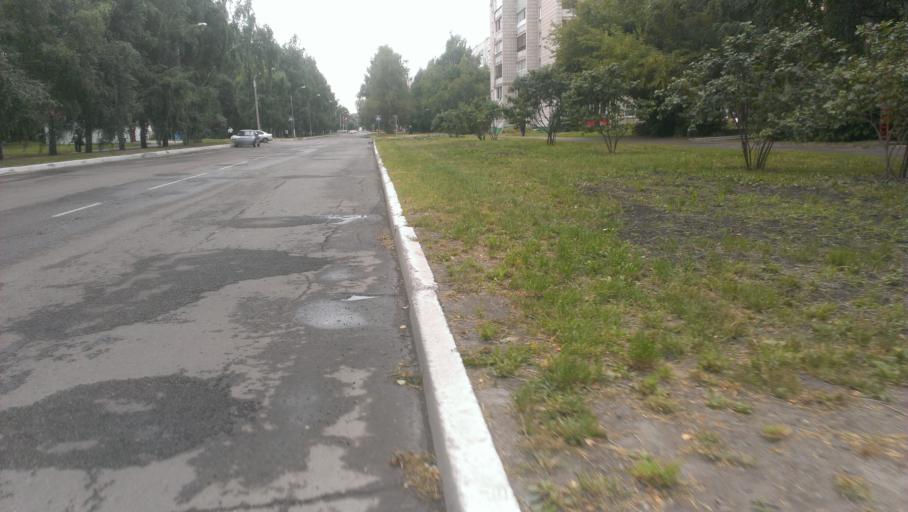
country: RU
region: Altai Krai
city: Novosilikatnyy
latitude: 53.3704
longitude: 83.6693
